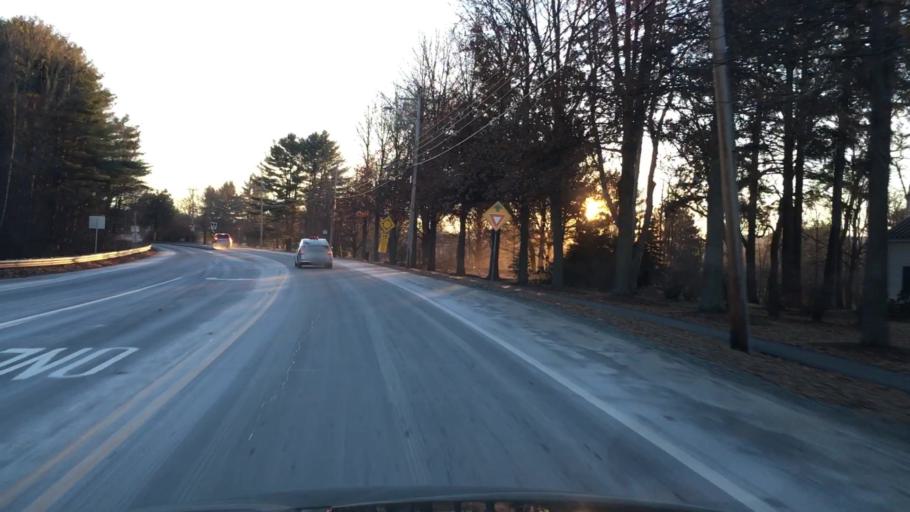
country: US
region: New Hampshire
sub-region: Grafton County
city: Hanover
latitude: 43.7288
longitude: -72.2679
